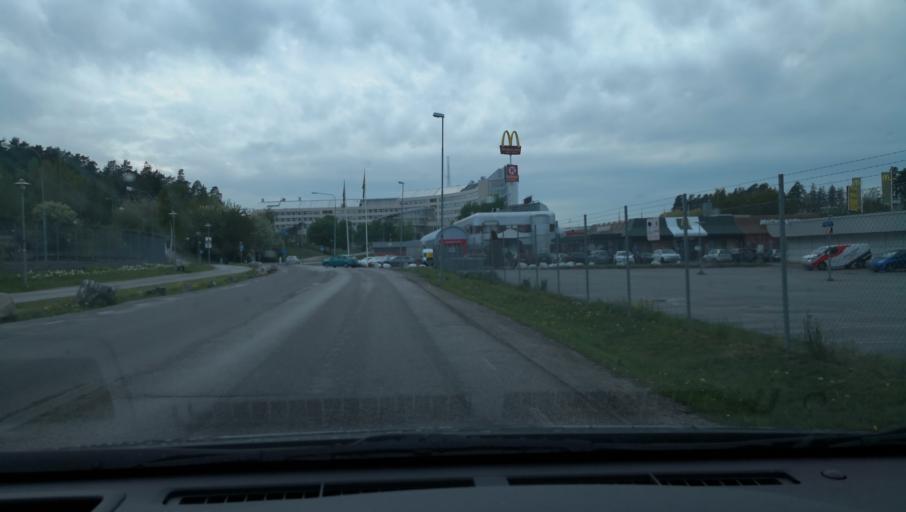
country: SE
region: Stockholm
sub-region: Stockholms Kommun
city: Kista
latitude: 59.3801
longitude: 17.9428
